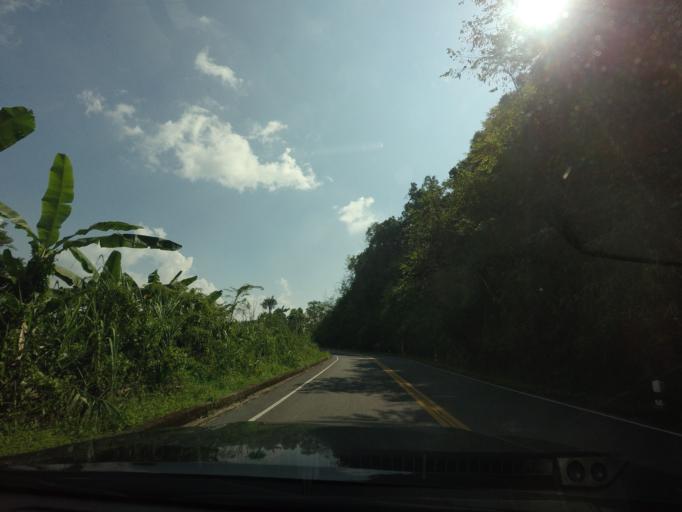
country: TH
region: Nan
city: Bo Kluea
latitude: 19.0588
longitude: 101.0912
